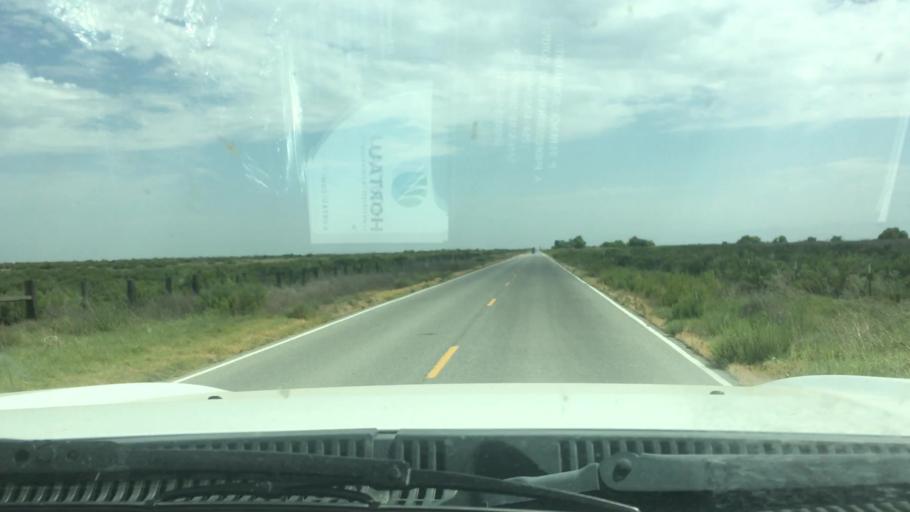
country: US
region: California
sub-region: Kern County
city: Lost Hills
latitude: 35.7427
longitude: -119.5795
